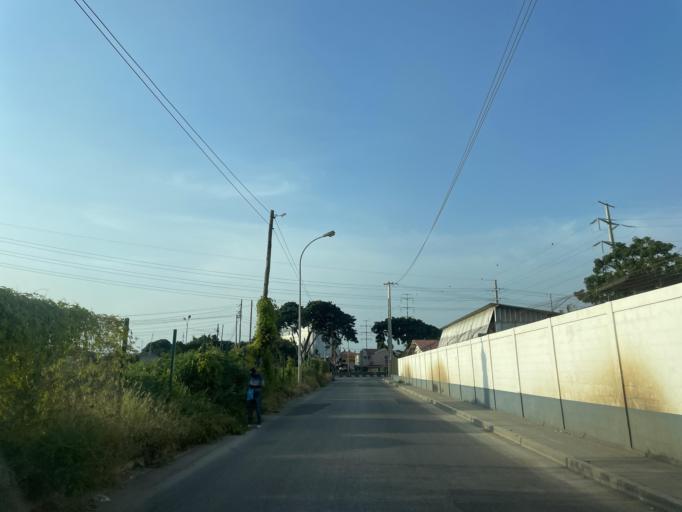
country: AO
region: Luanda
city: Luanda
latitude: -8.9068
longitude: 13.1838
